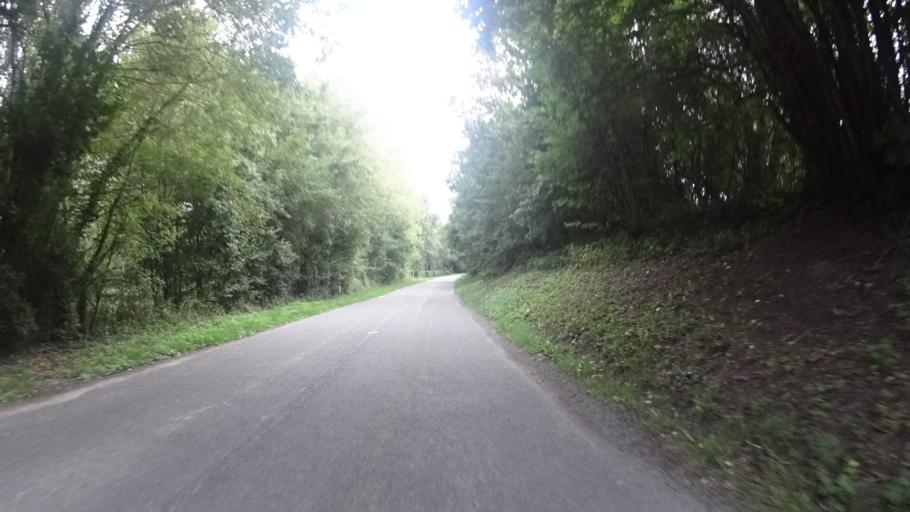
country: FR
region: Picardie
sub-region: Departement de l'Aisne
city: Guise
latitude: 49.8920
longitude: 3.5559
